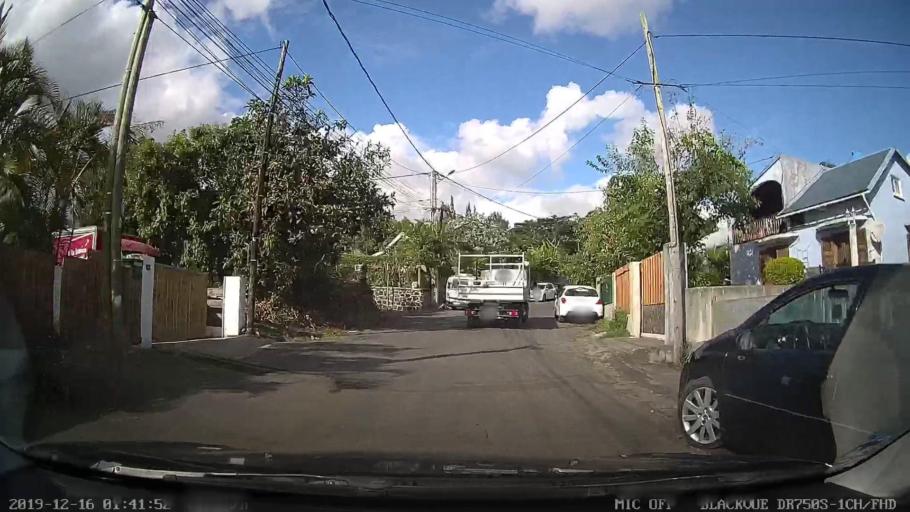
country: RE
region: Reunion
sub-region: Reunion
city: Le Tampon
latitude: -21.2548
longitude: 55.5100
